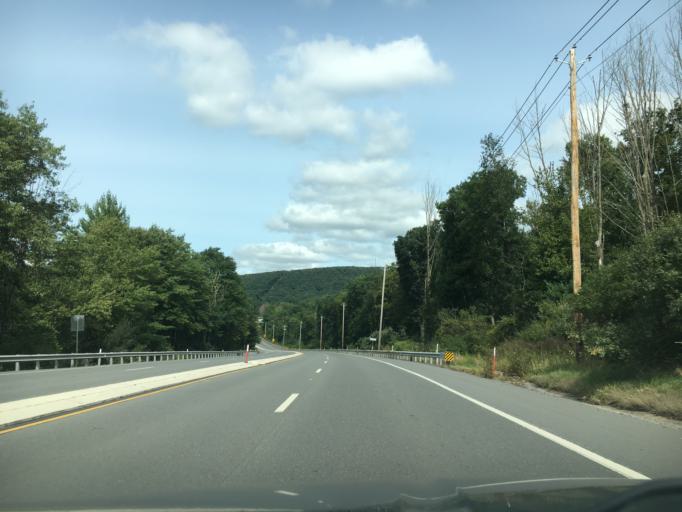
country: US
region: Pennsylvania
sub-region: Schuylkill County
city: Hometown
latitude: 40.8503
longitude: -75.9975
